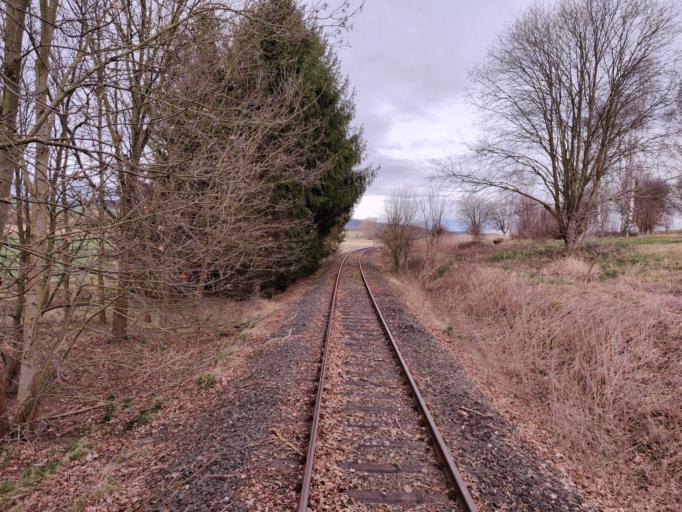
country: DE
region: Lower Saxony
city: Bockenem
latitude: 52.0261
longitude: 10.1248
